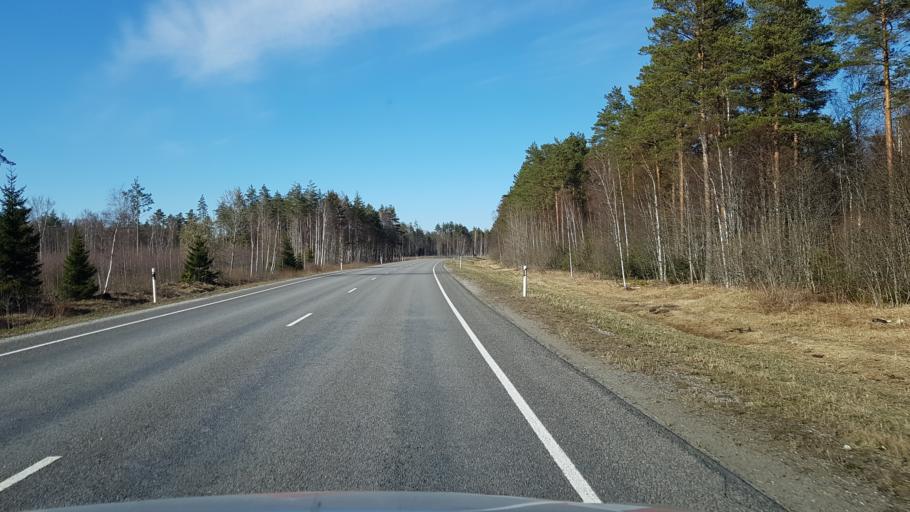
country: EE
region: Jogevamaa
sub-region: Mustvee linn
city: Mustvee
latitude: 59.0197
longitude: 27.2250
